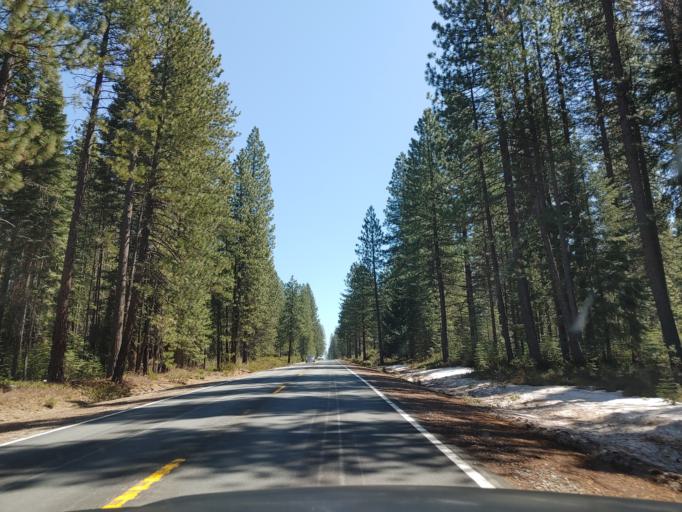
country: US
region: California
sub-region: Siskiyou County
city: McCloud
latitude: 41.2668
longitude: -121.8929
